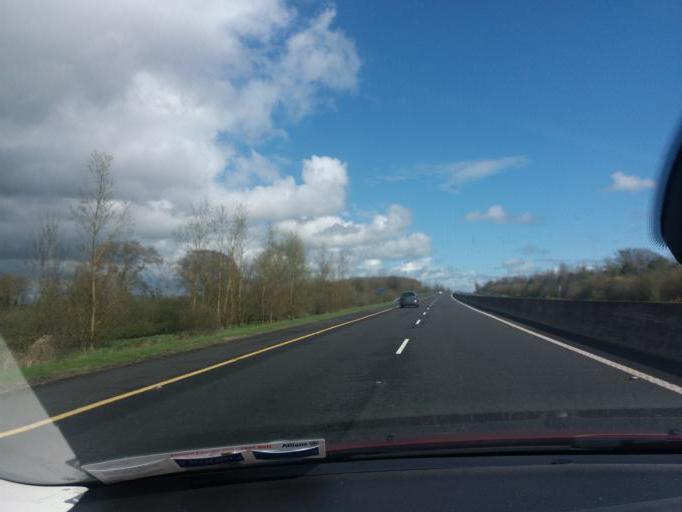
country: IE
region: Munster
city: Thurles
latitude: 52.6875
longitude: -7.6710
